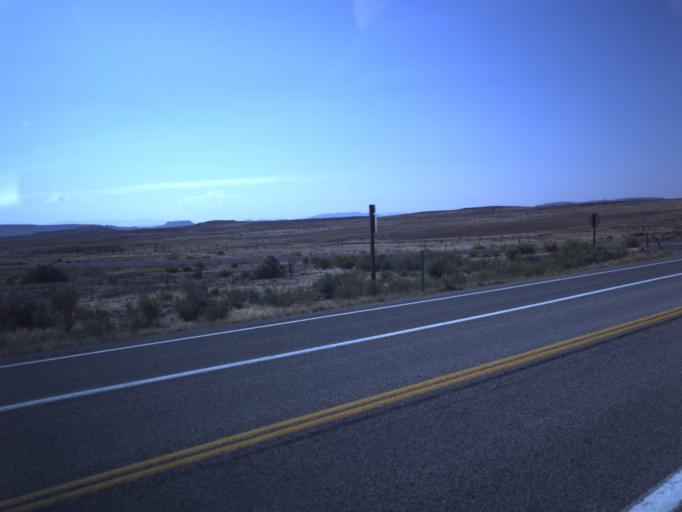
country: US
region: Utah
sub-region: San Juan County
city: Blanding
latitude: 37.4239
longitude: -109.4737
